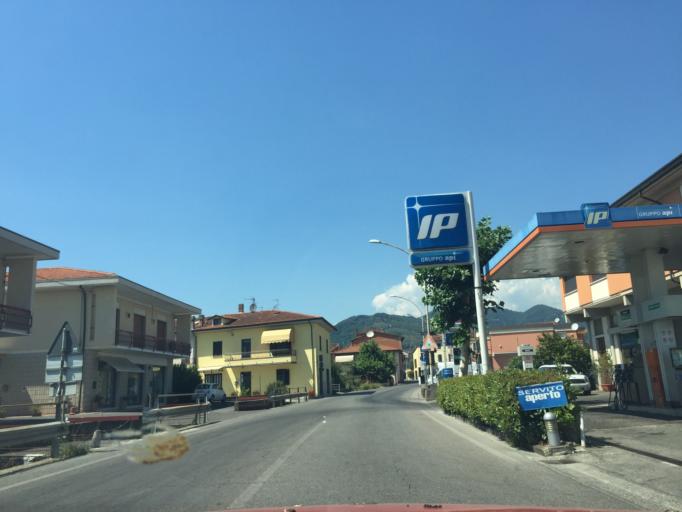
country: IT
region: Tuscany
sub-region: Provincia di Pistoia
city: Pescia
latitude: 43.8781
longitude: 10.6889
